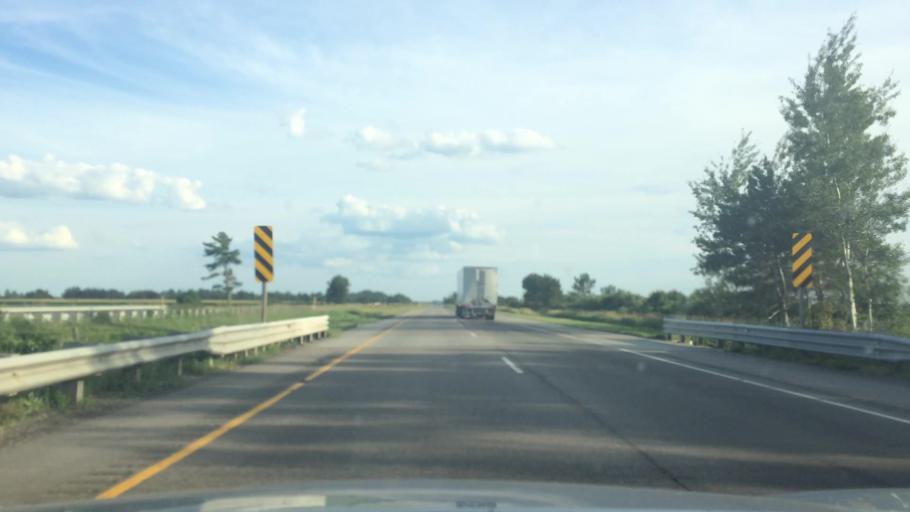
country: US
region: Wisconsin
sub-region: Portage County
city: Plover
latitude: 44.3891
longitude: -89.5198
